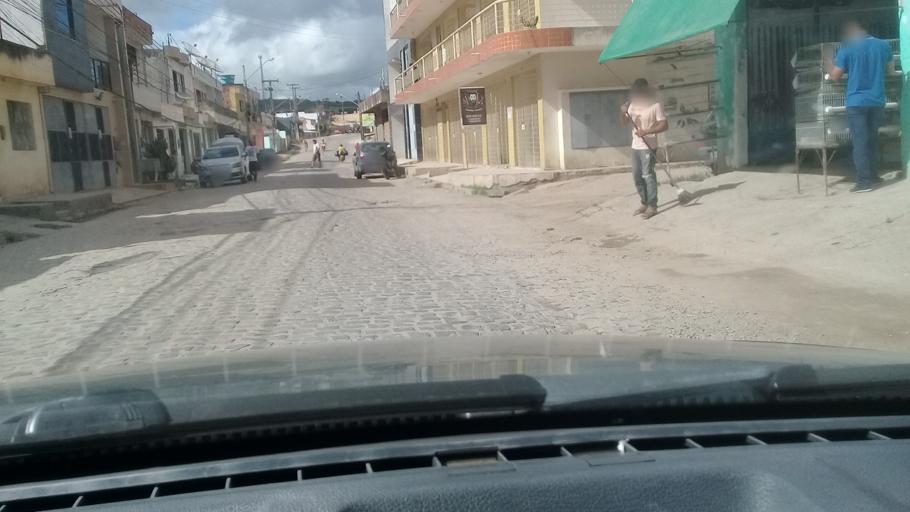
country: BR
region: Pernambuco
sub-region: Vitoria De Santo Antao
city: Vitoria de Santo Antao
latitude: -8.1268
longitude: -35.2962
